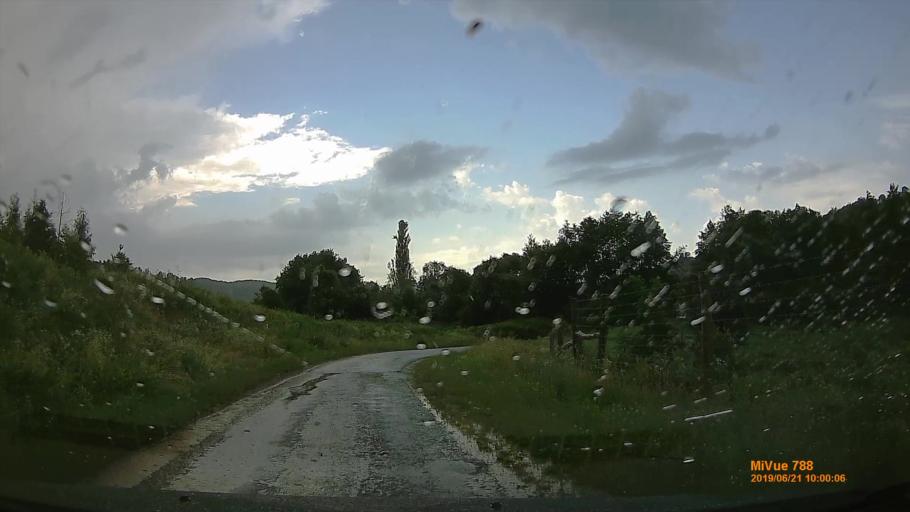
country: HU
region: Baranya
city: Buekkoesd
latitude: 46.2090
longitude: 17.9731
